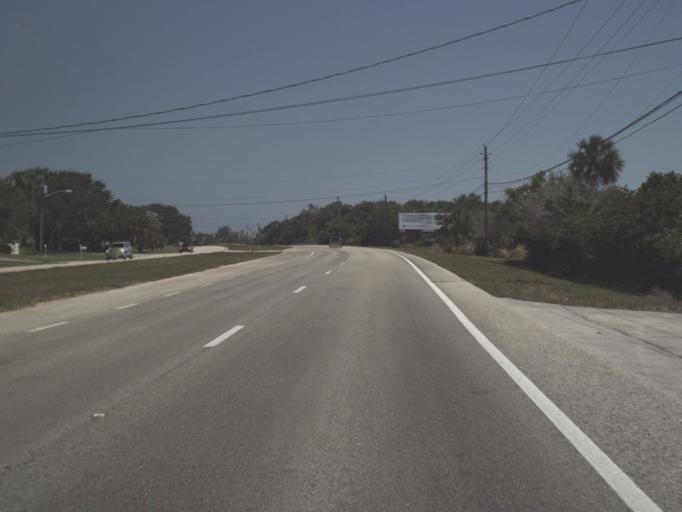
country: US
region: Florida
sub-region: Brevard County
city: Micco
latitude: 27.9124
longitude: -80.5174
